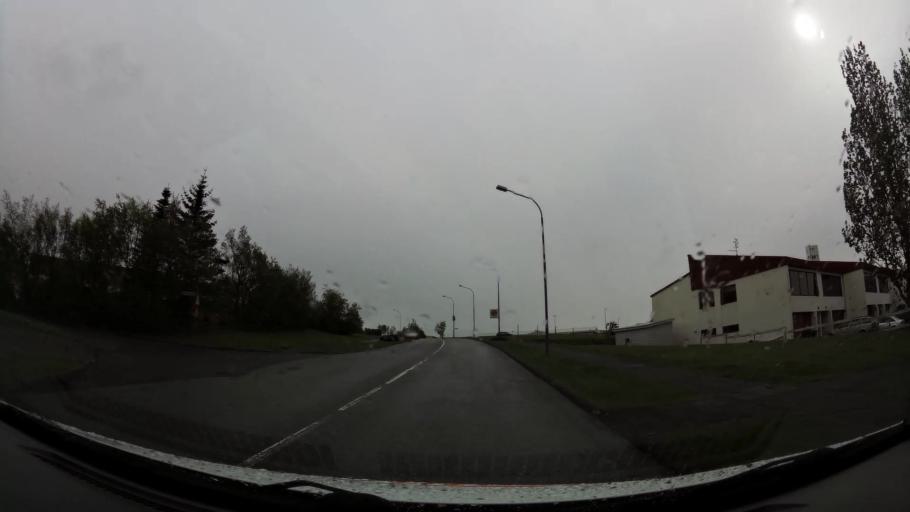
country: IS
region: Capital Region
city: Gardabaer
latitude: 64.0893
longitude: -21.9135
